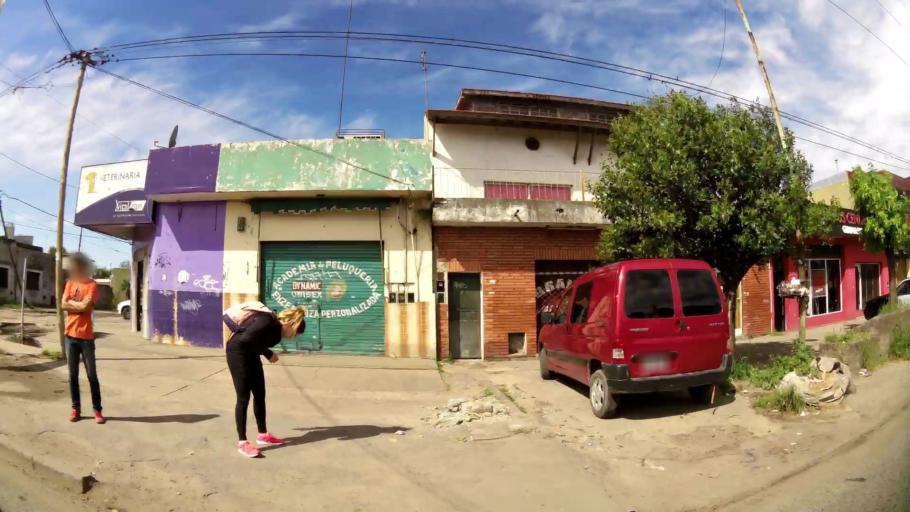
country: AR
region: Buenos Aires
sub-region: Partido de Almirante Brown
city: Adrogue
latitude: -34.7899
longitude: -58.3121
